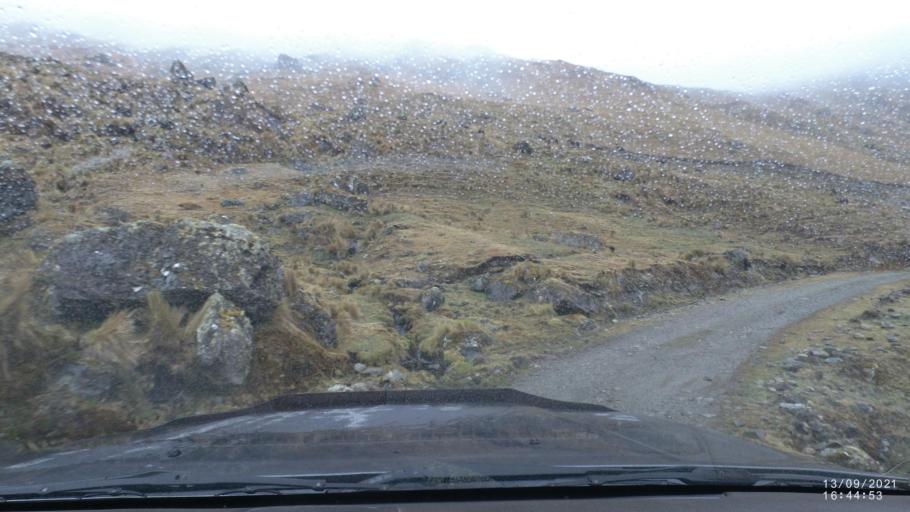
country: BO
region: Cochabamba
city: Colomi
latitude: -17.2940
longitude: -65.7103
